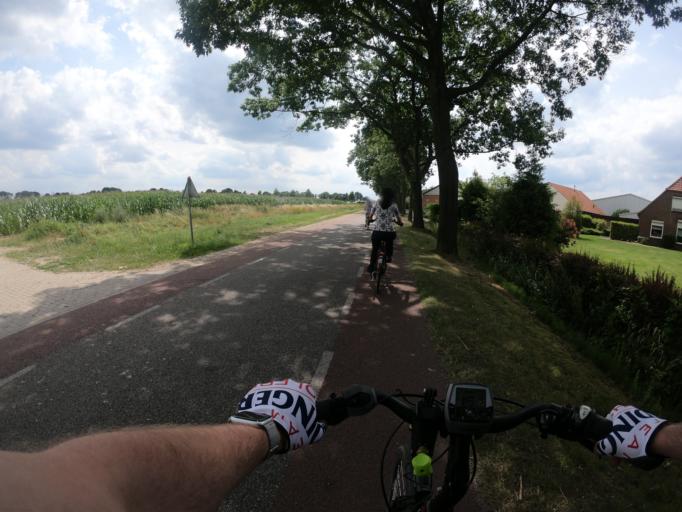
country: NL
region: Gelderland
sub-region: Gemeente Groesbeek
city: De Horst
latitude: 51.7780
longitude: 5.9556
